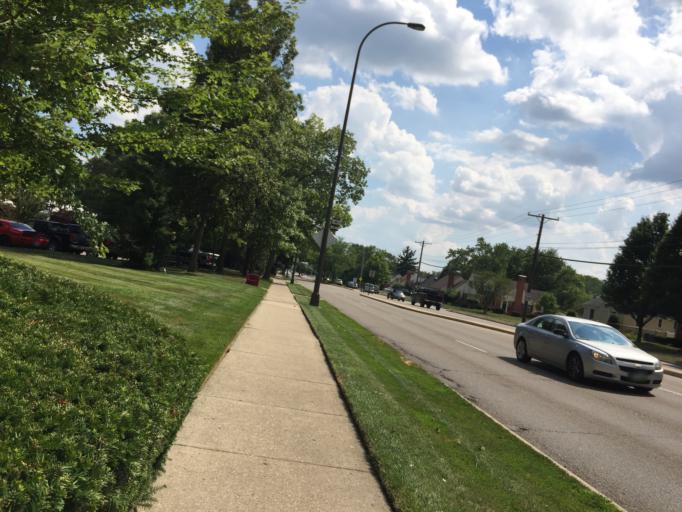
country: US
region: Ohio
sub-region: Montgomery County
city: Kettering
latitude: 39.6967
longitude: -84.1628
